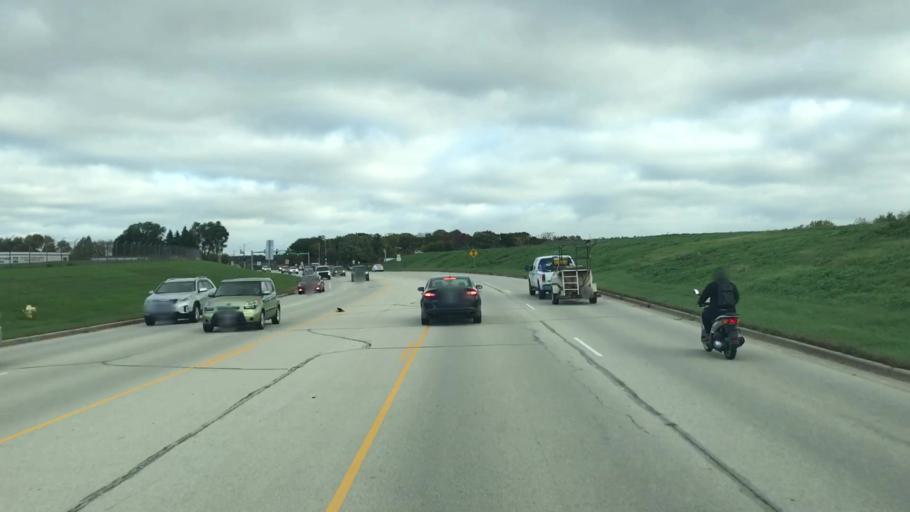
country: US
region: Wisconsin
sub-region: Waukesha County
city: Waukesha
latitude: 43.0393
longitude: -88.2255
